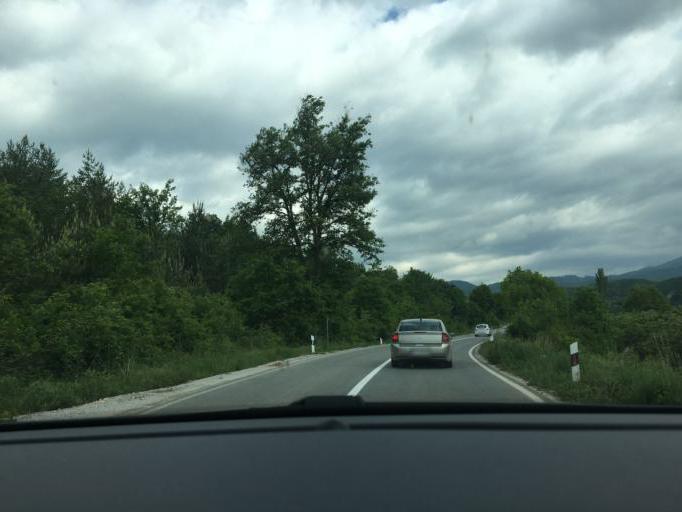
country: MK
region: Resen
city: Jankovec
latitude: 41.1233
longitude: 21.0083
